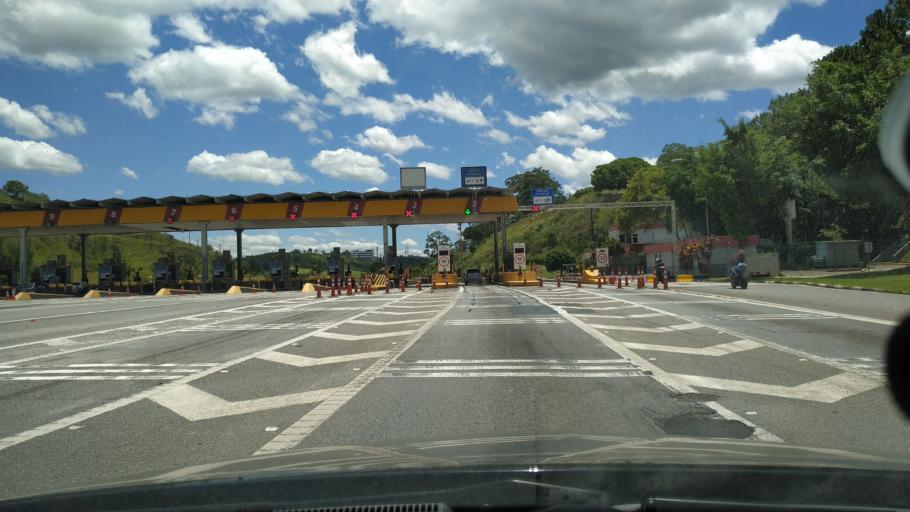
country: BR
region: Sao Paulo
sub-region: Itapevi
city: Itapevi
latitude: -23.5176
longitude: -46.9403
